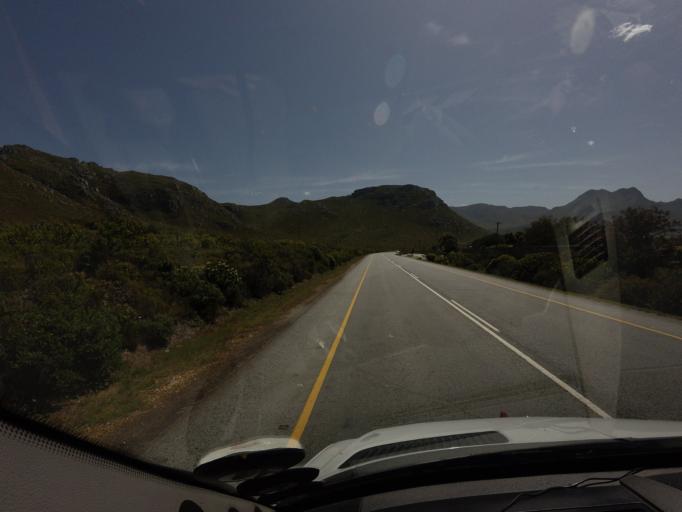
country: ZA
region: Western Cape
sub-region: Overberg District Municipality
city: Grabouw
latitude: -34.3483
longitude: 18.9750
